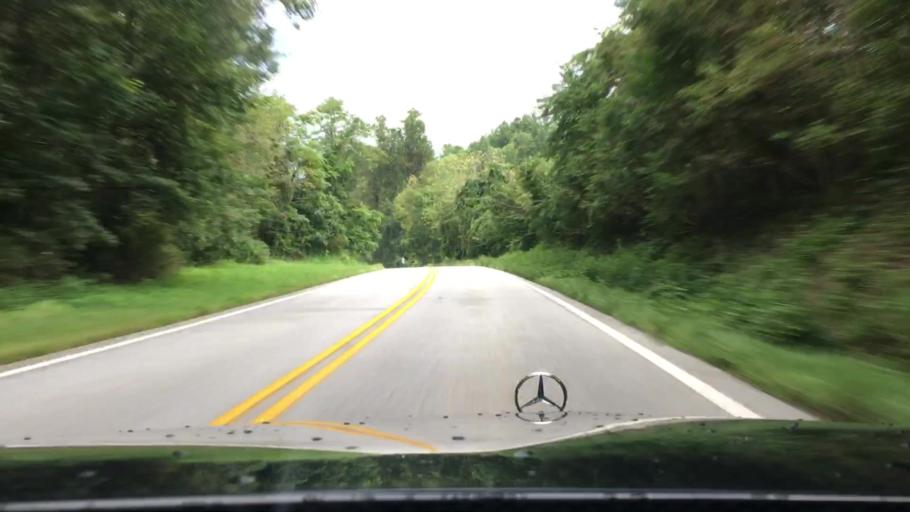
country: US
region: Virginia
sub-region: Nelson County
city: Nellysford
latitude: 37.8296
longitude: -78.9342
